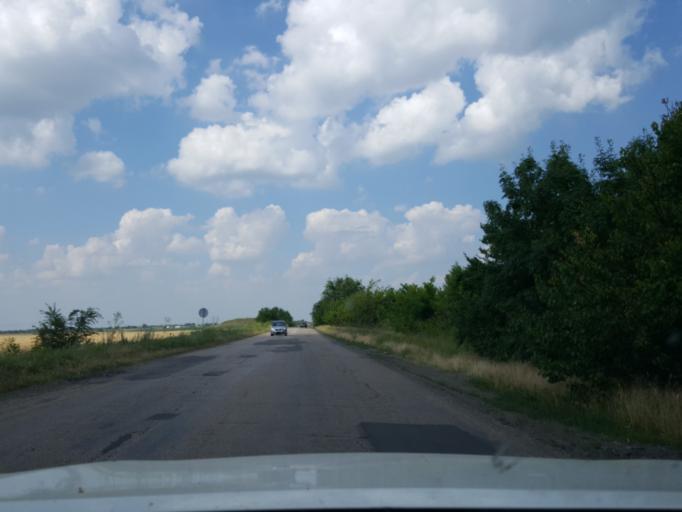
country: UA
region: Odessa
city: Starokozache
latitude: 46.3869
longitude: 30.0886
